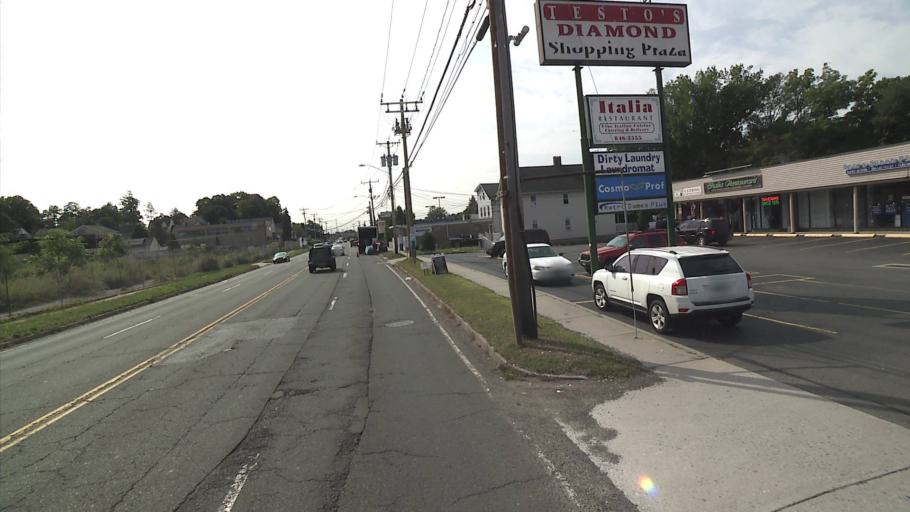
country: US
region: Connecticut
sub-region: Fairfield County
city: Norwalk
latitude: 41.1336
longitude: -73.4243
